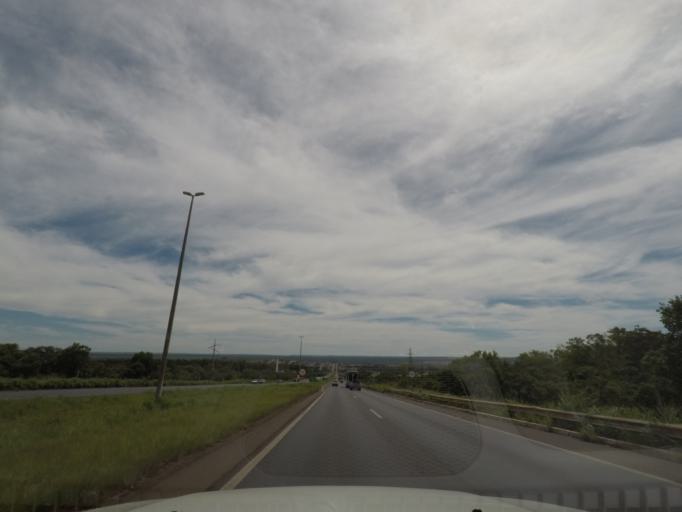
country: BR
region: Goias
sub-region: Planaltina
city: Planaltina
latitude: -15.6174
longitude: -47.7099
